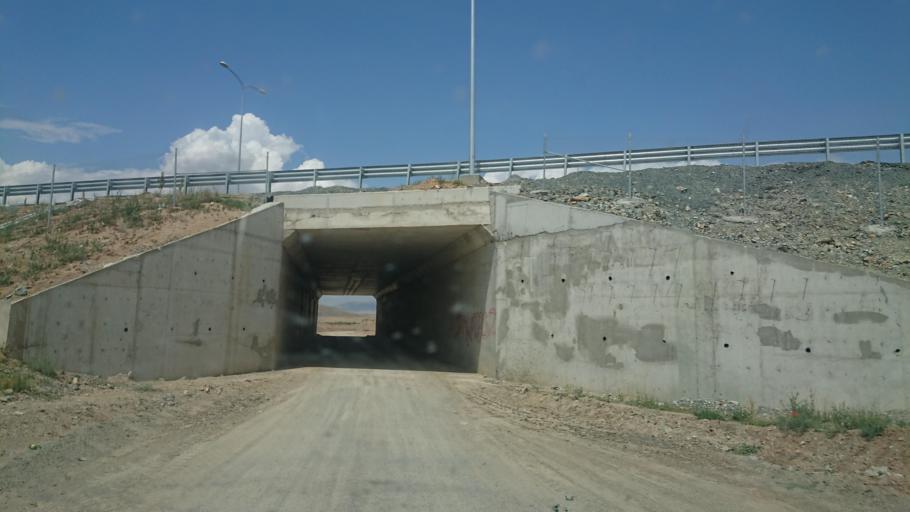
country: TR
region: Aksaray
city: Sariyahsi
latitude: 38.9739
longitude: 33.8991
